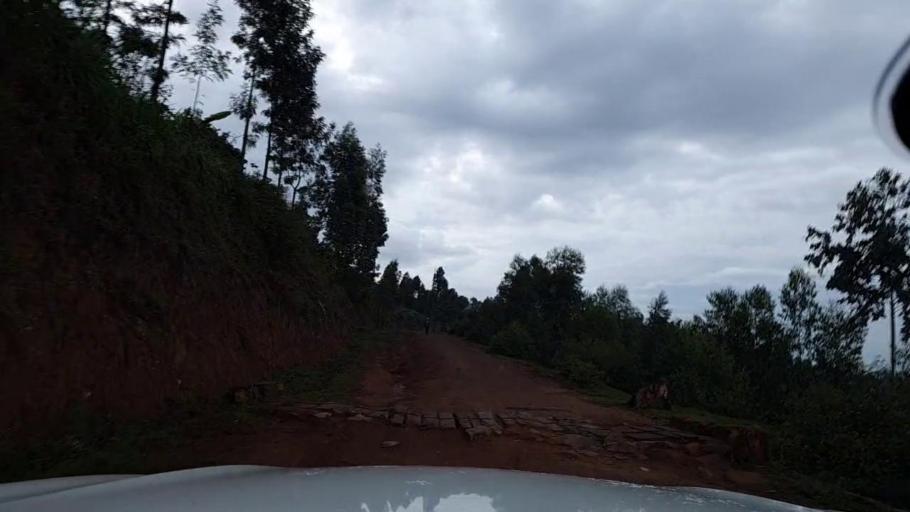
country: BI
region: Kayanza
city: Kayanza
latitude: -2.7169
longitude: 29.5435
